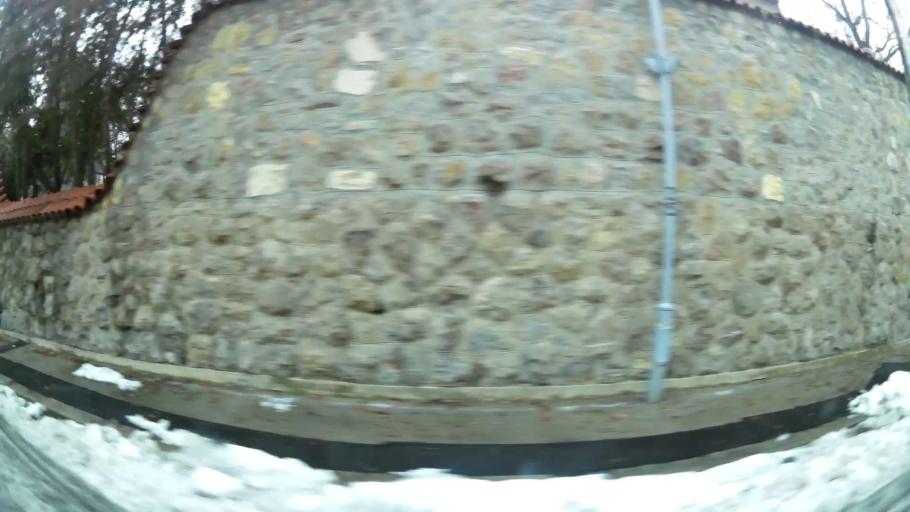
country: RS
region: Central Serbia
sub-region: Belgrade
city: Savski Venac
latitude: 44.7820
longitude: 20.4524
